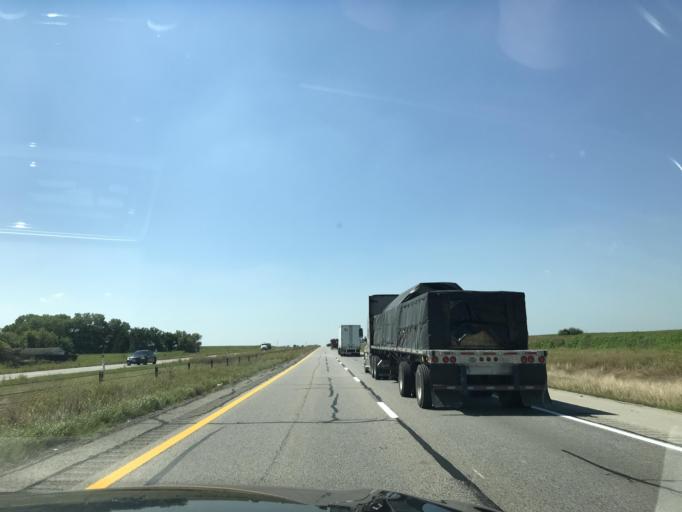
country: US
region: Texas
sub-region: Johnson County
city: Grandview
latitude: 32.3369
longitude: -97.1912
